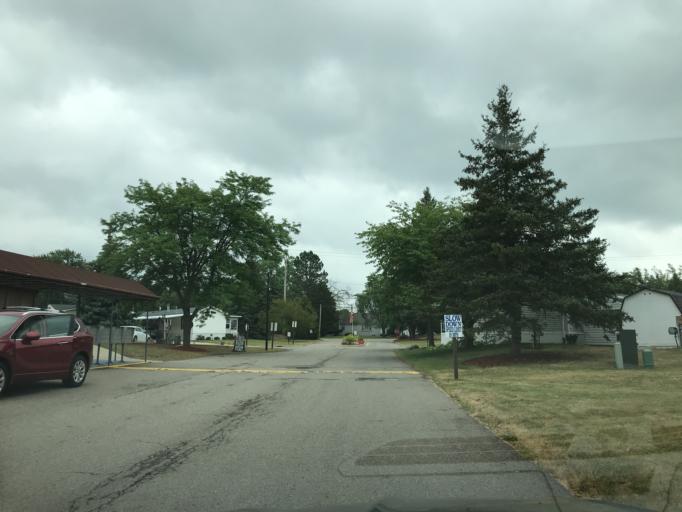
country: US
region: Michigan
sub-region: Eaton County
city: Waverly
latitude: 42.7351
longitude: -84.6635
